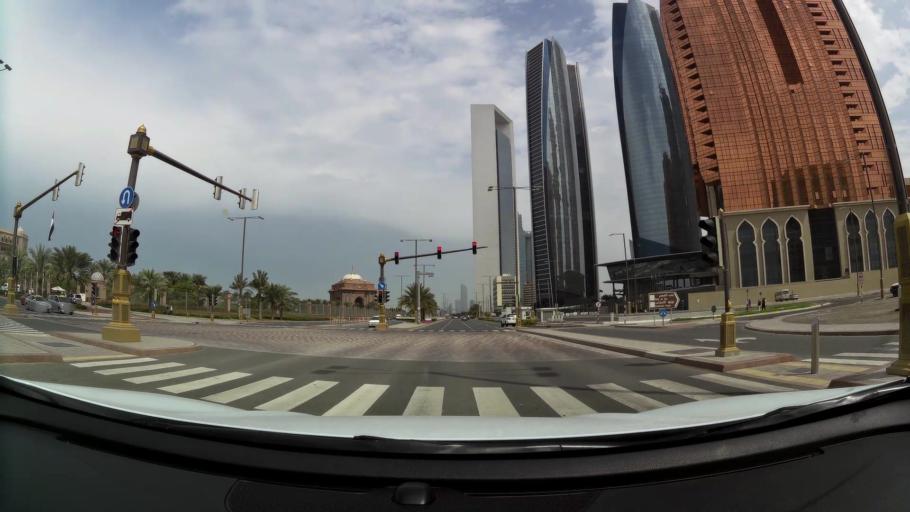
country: AE
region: Abu Dhabi
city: Abu Dhabi
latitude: 24.4581
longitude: 54.3186
